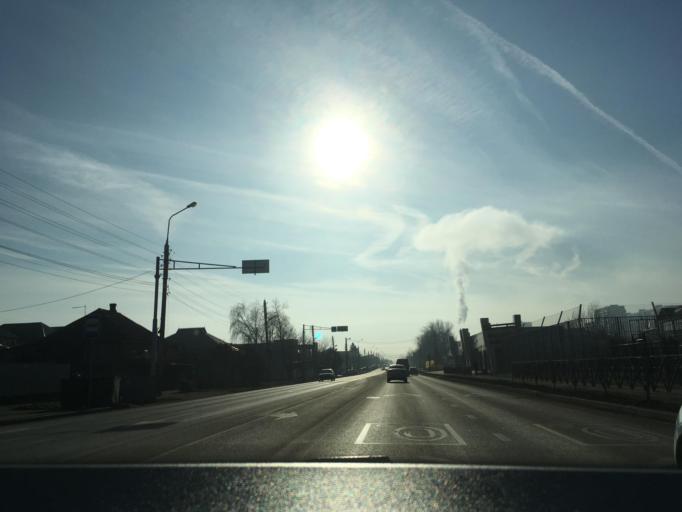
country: RU
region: Krasnodarskiy
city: Krasnodar
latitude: 45.0997
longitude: 39.0132
